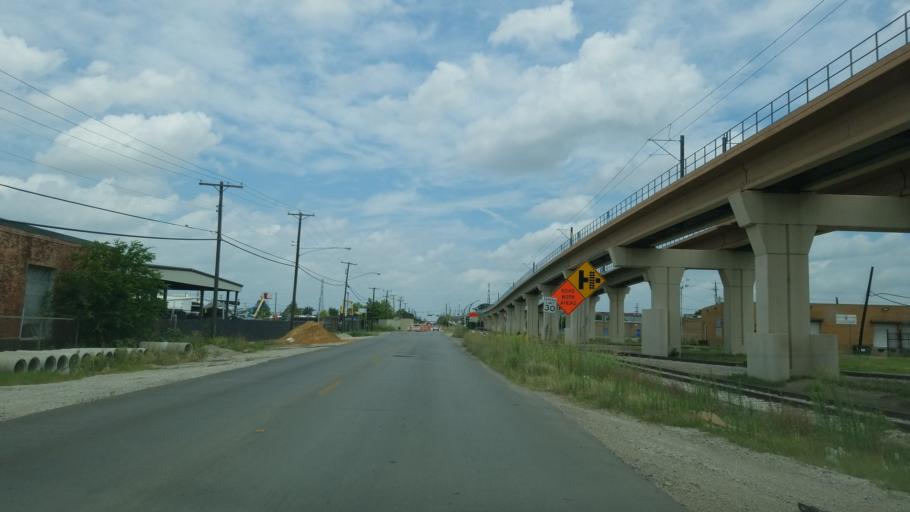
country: US
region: Texas
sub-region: Dallas County
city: Farmers Branch
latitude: 32.8786
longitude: -96.8831
